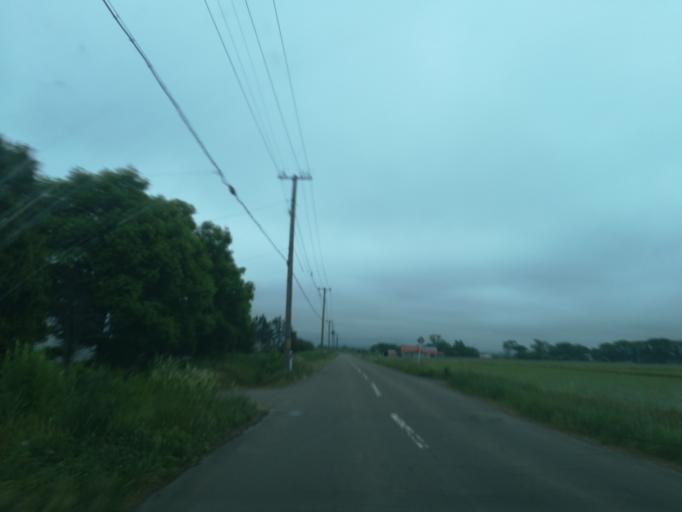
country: JP
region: Hokkaido
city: Iwamizawa
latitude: 43.1263
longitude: 141.6915
